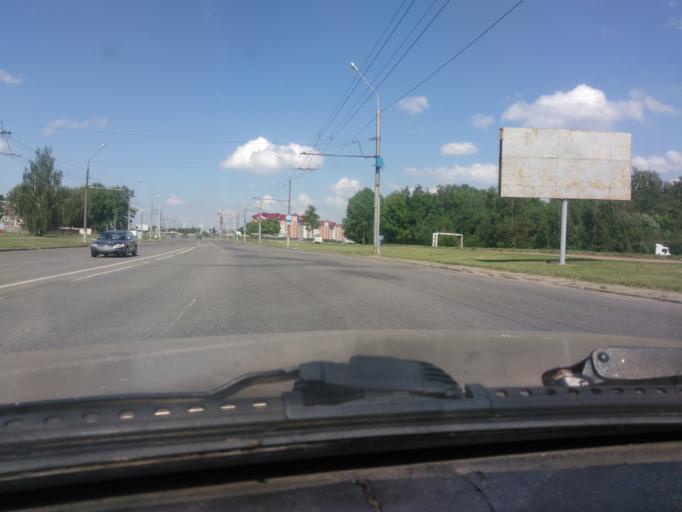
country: BY
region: Mogilev
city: Palykavichy Pyershyya
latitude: 53.9573
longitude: 30.3635
